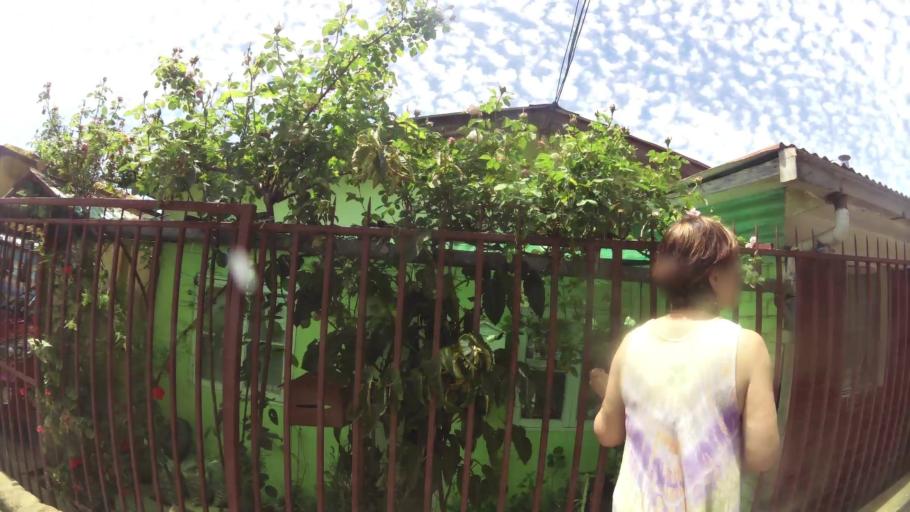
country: CL
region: Valparaiso
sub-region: Provincia de Valparaiso
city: Vina del Mar
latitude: -33.0514
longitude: -71.5656
